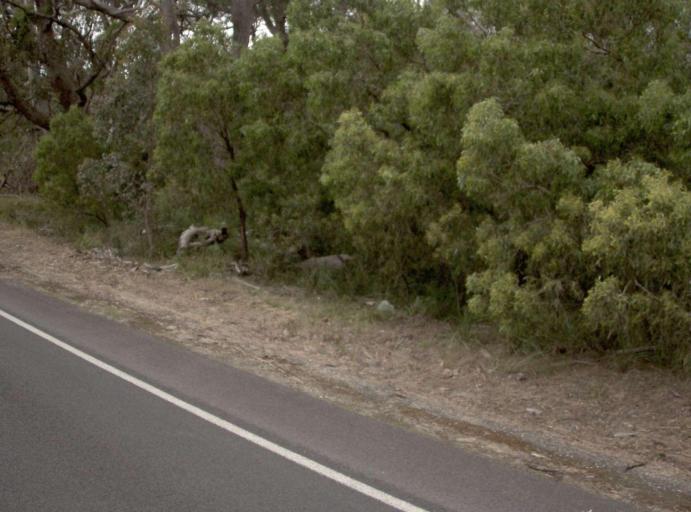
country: AU
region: Victoria
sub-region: Wellington
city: Sale
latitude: -38.2357
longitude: 147.0545
